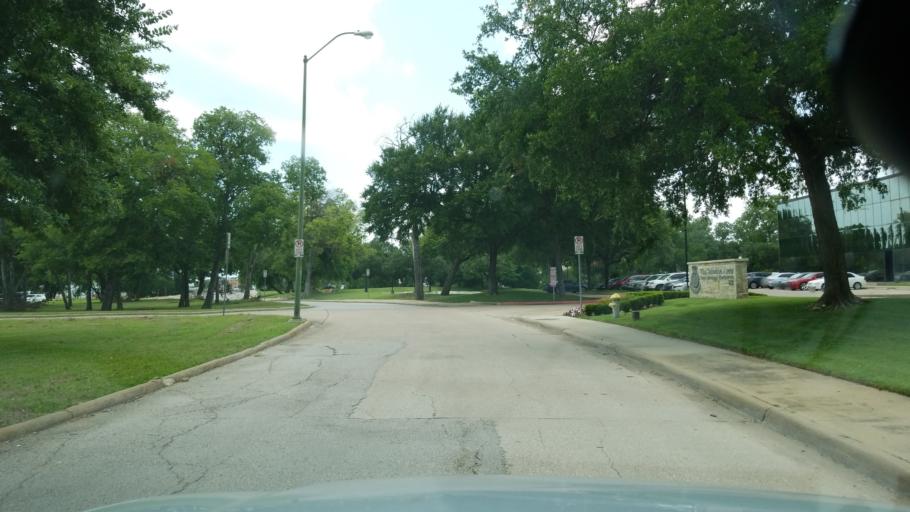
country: US
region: Texas
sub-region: Dallas County
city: Dallas
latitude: 32.8170
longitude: -96.8641
